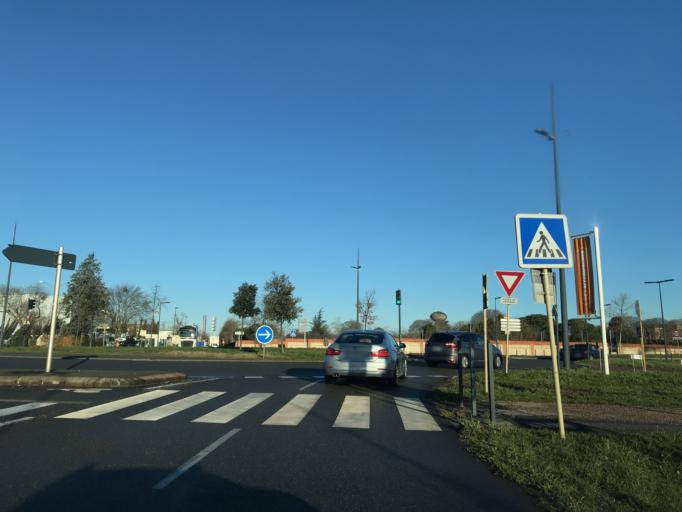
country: FR
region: Midi-Pyrenees
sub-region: Departement de la Haute-Garonne
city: Vieille-Toulouse
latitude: 43.5554
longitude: 1.4242
